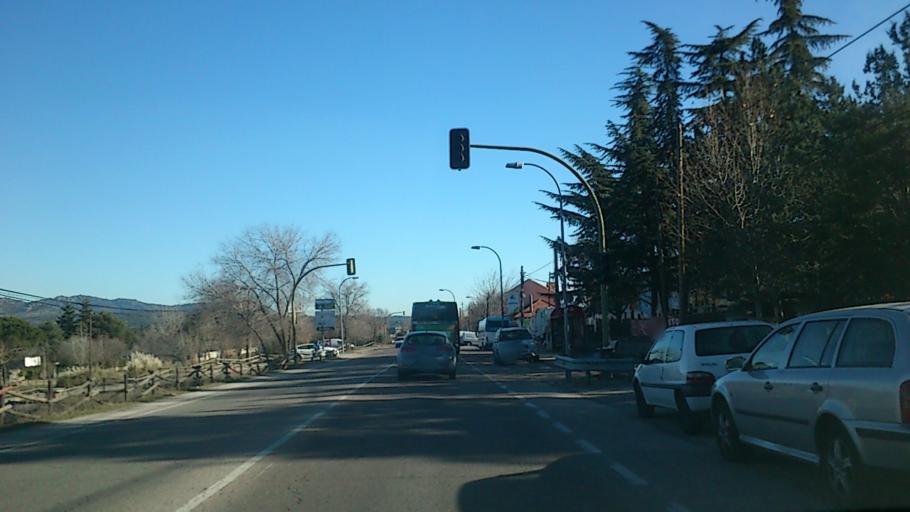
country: ES
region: Madrid
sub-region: Provincia de Madrid
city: Alpedrete
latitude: 40.6400
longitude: -4.0287
